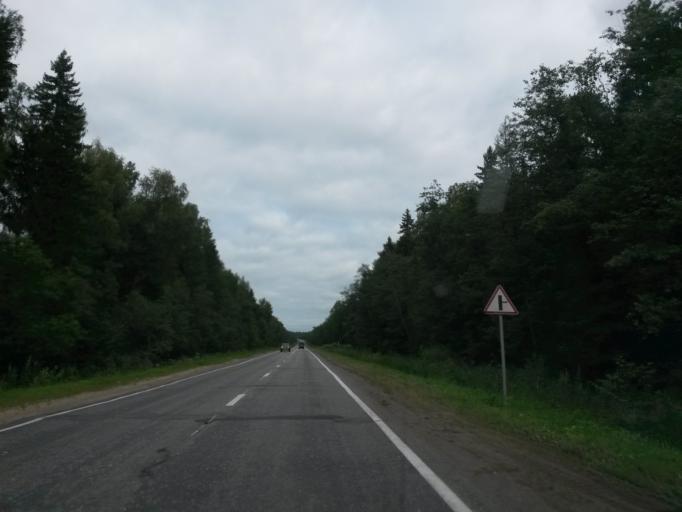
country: RU
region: Jaroslavl
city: Gavrilov-Yam
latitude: 57.4287
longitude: 39.9187
